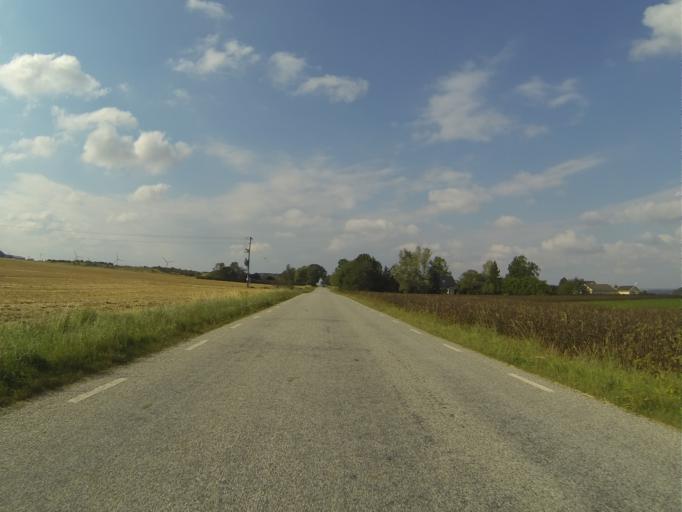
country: SE
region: Skane
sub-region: Lunds Kommun
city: Lund
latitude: 55.7344
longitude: 13.2911
